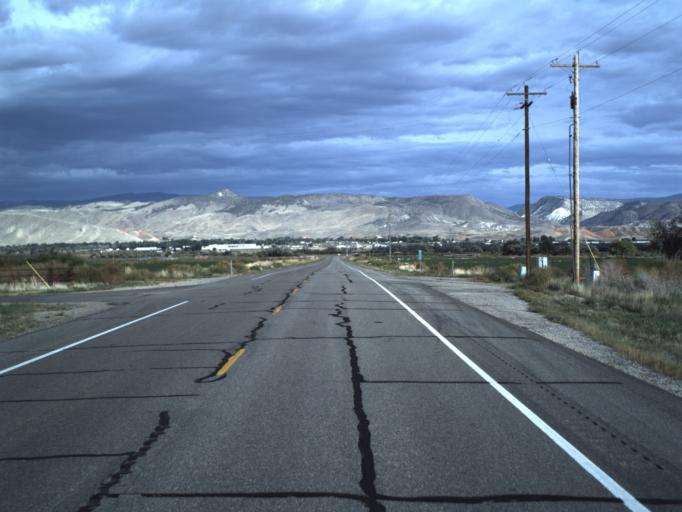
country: US
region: Utah
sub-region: Sevier County
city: Aurora
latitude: 38.9545
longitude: -111.9052
